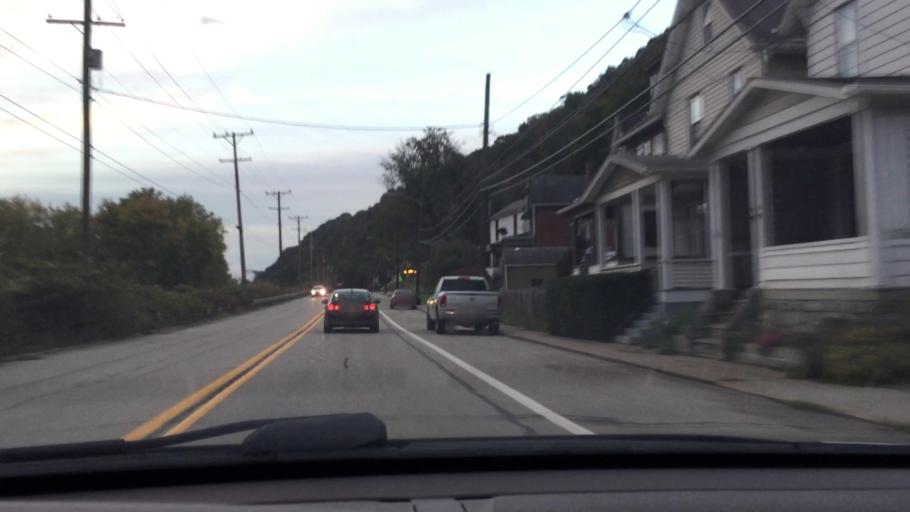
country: US
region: Pennsylvania
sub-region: Westmoreland County
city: New Kensington
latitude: 40.5723
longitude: -79.7772
